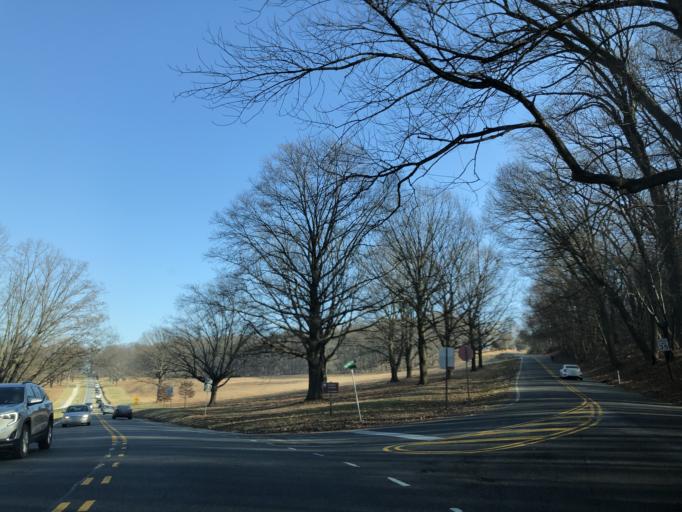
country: US
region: Pennsylvania
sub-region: Chester County
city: Chesterbrook
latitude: 40.0998
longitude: -75.4593
